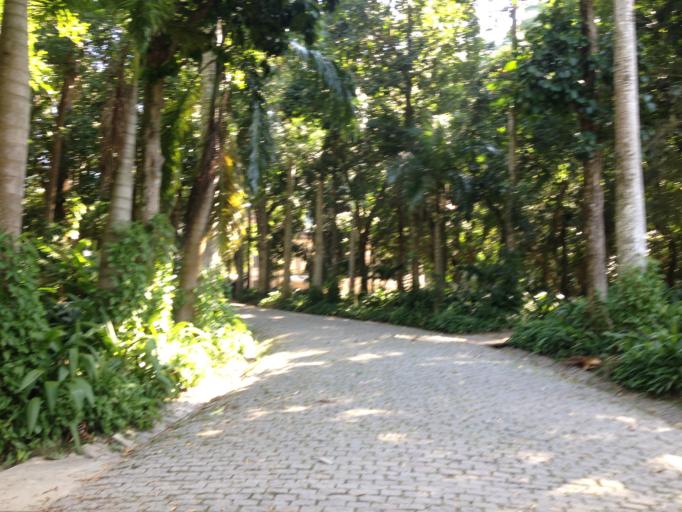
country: BR
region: Rio de Janeiro
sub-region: Rio De Janeiro
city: Rio de Janeiro
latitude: -22.9604
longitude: -43.2112
